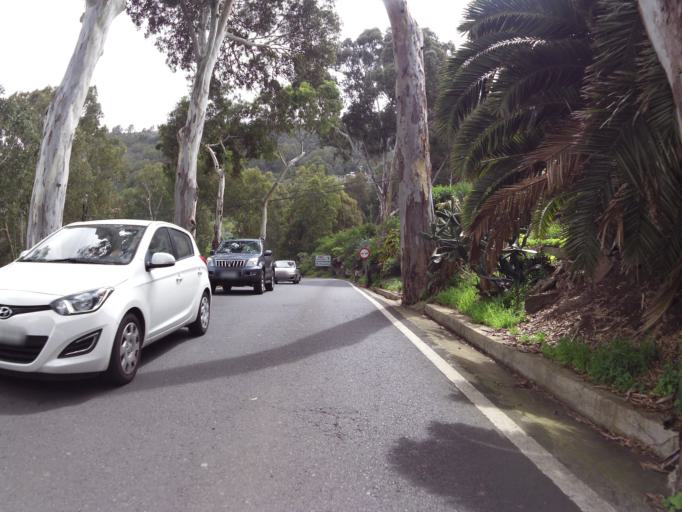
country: ES
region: Canary Islands
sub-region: Provincia de Las Palmas
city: Arucas
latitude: 28.0984
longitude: -15.5317
